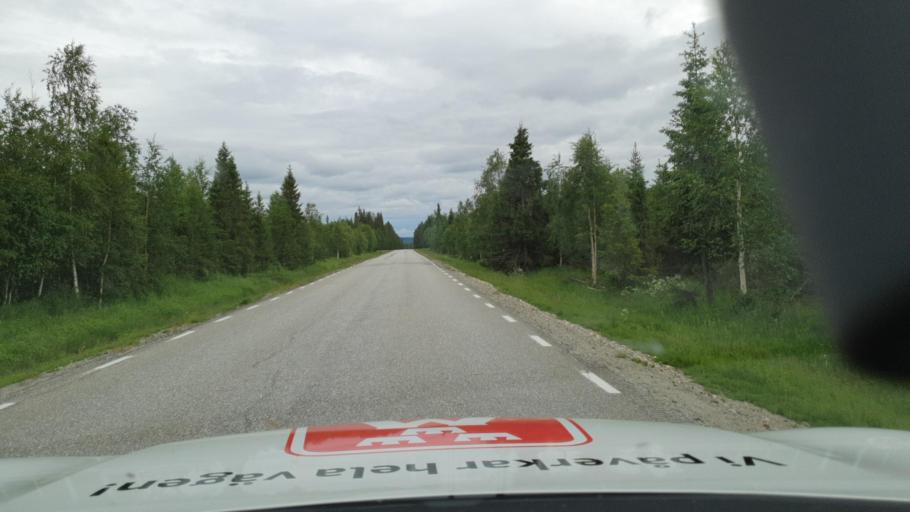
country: SE
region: Vaesterbotten
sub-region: Lycksele Kommun
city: Soderfors
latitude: 64.3144
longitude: 18.1595
